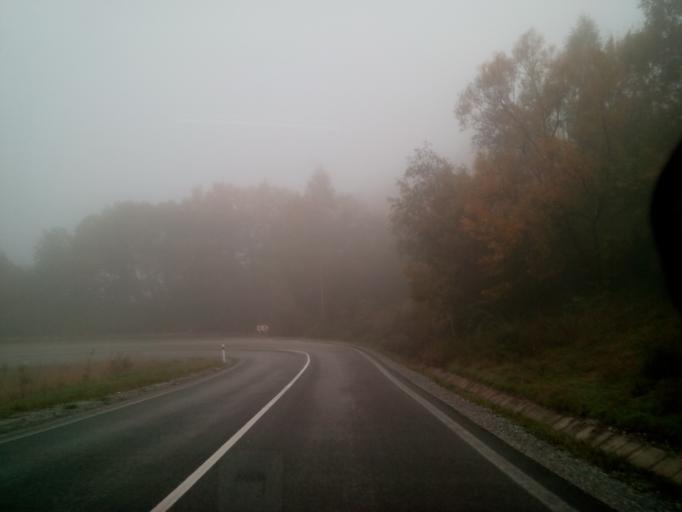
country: SK
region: Kosicky
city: Gelnica
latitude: 48.8534
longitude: 21.0275
